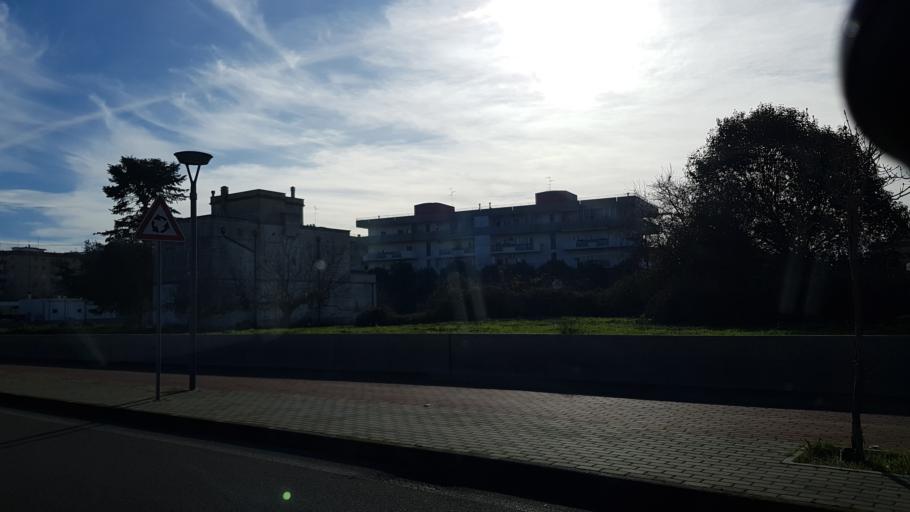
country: IT
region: Apulia
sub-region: Provincia di Bari
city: Gioia del Colle
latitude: 40.8010
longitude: 16.9137
